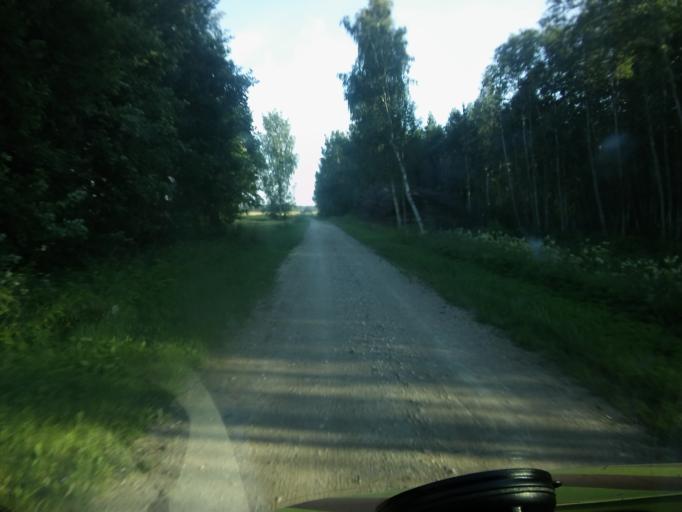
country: EE
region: Valgamaa
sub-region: Torva linn
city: Torva
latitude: 58.0939
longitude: 25.9947
